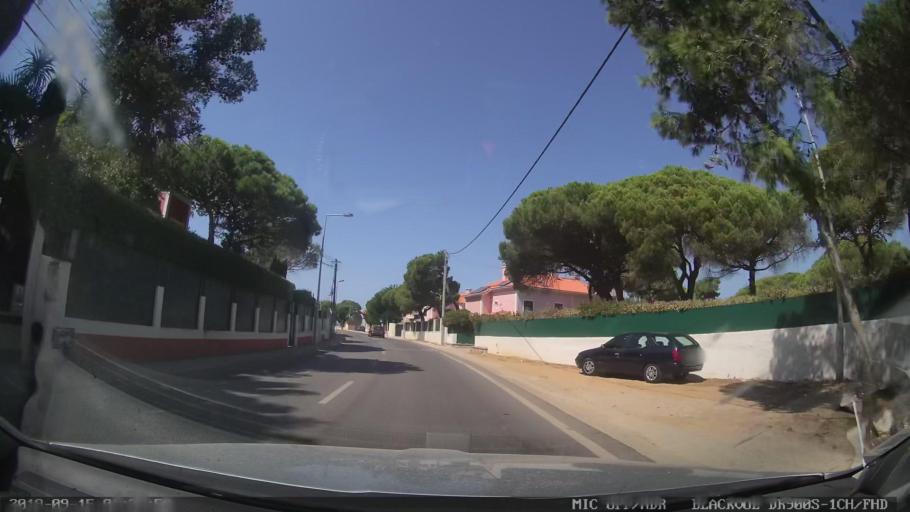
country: PT
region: Lisbon
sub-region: Cascais
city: Cascais
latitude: 38.7161
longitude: -9.4527
